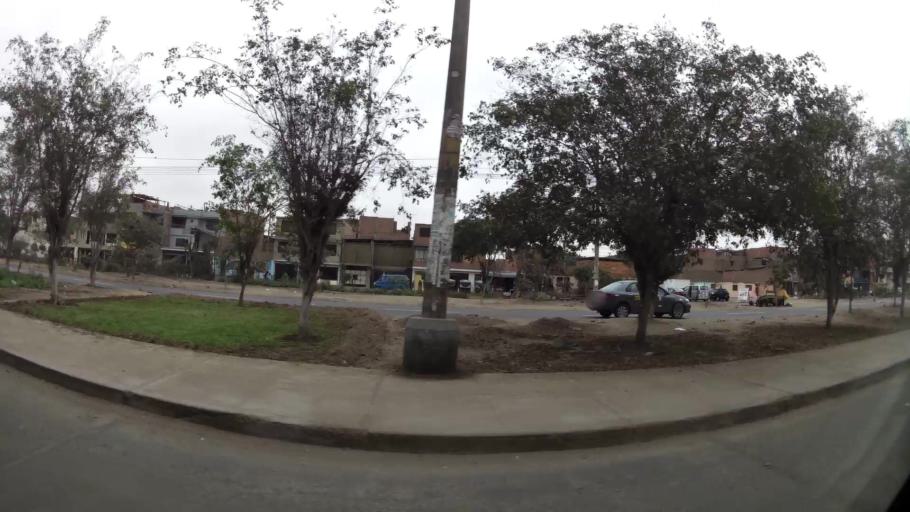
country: PE
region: Lima
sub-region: Lima
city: Independencia
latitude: -11.9717
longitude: -77.0602
